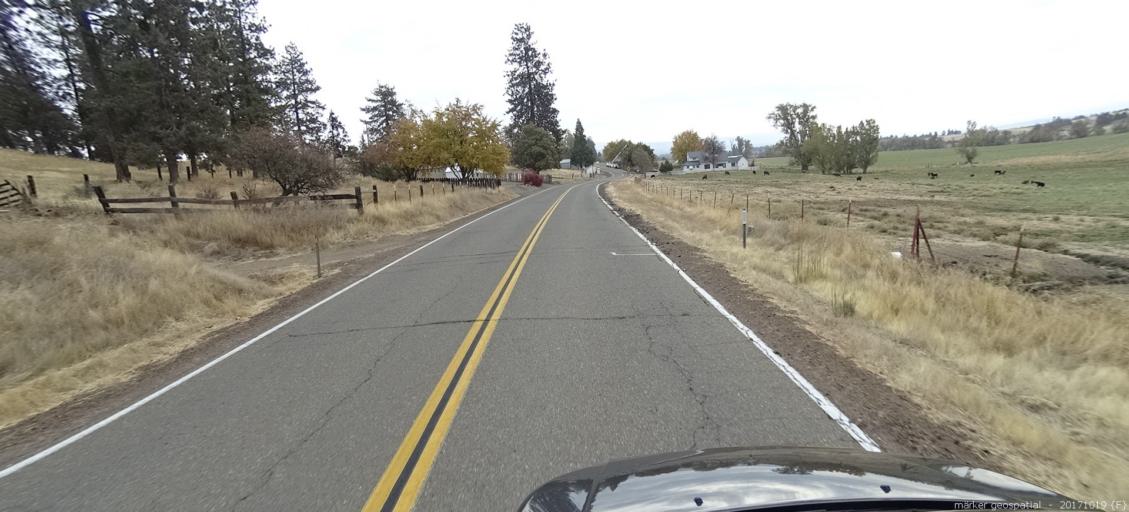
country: US
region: California
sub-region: Shasta County
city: Burney
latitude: 41.0545
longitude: -121.3623
